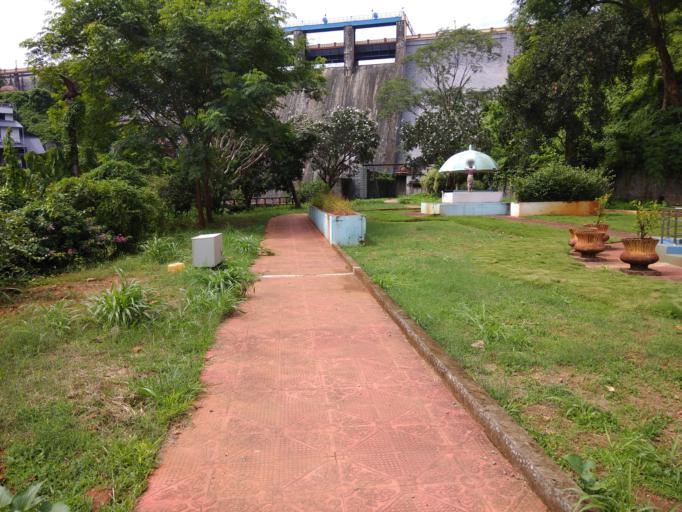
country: IN
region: Kerala
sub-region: Thrissur District
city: Trichur
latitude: 10.5310
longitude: 76.3693
